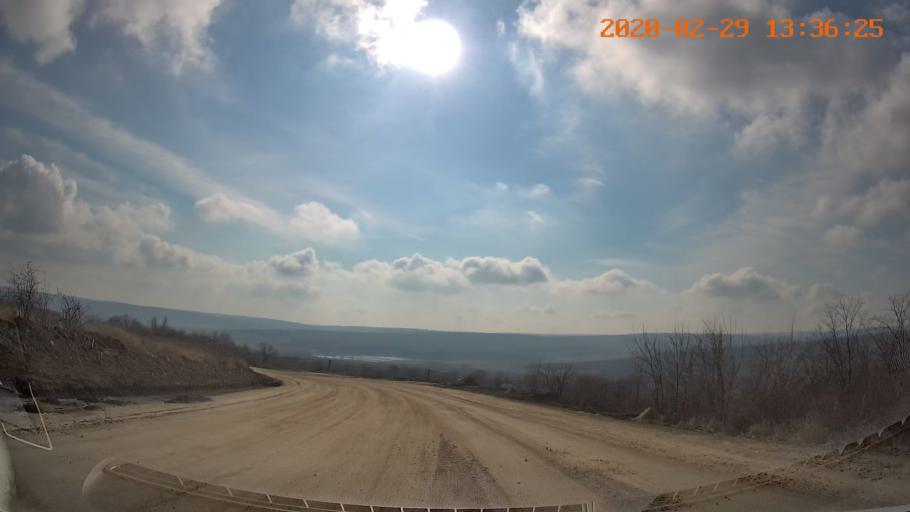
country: MD
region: Telenesti
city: Camenca
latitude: 47.8618
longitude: 28.6061
